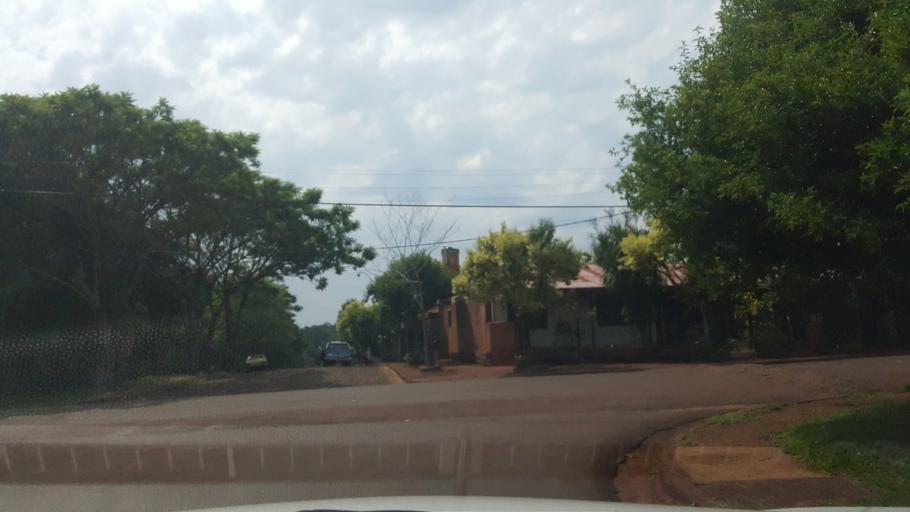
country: AR
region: Misiones
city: Capiovi
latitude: -26.9321
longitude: -55.0556
